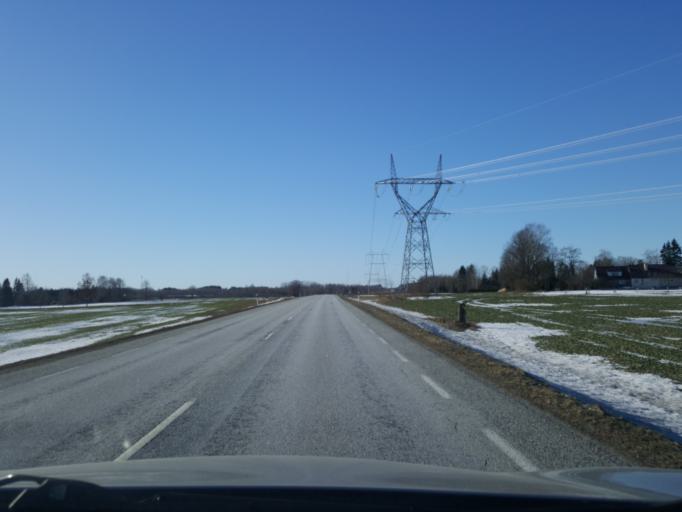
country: EE
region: Viljandimaa
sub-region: Viiratsi vald
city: Viiratsi
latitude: 58.3892
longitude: 25.6202
